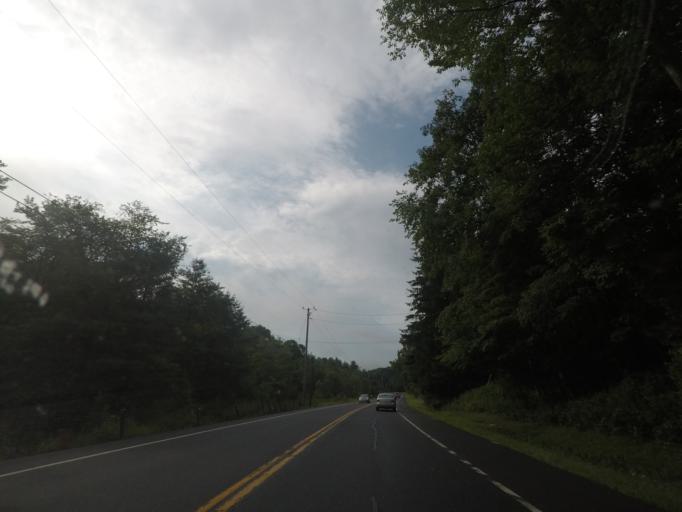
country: US
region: New York
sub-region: Rensselaer County
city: Nassau
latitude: 42.5067
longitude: -73.5620
